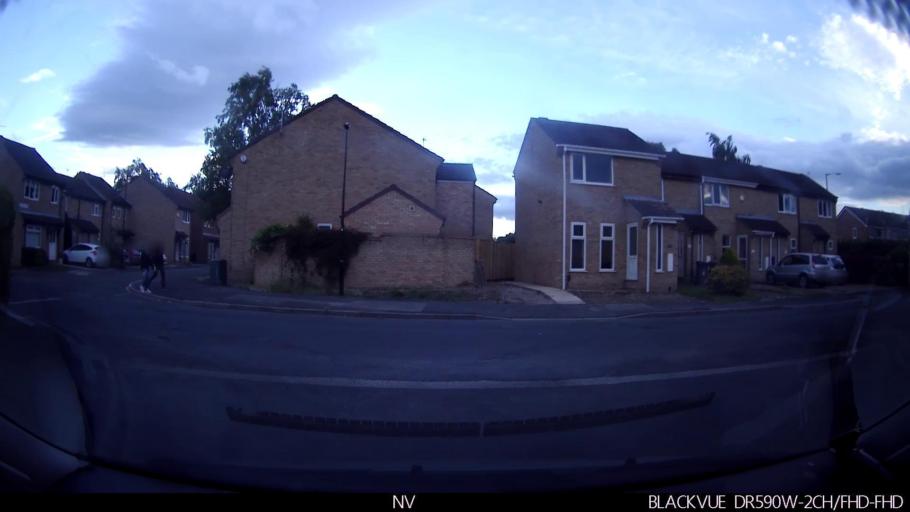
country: GB
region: England
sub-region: City of York
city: Copmanthorpe
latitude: 53.9416
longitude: -1.1345
